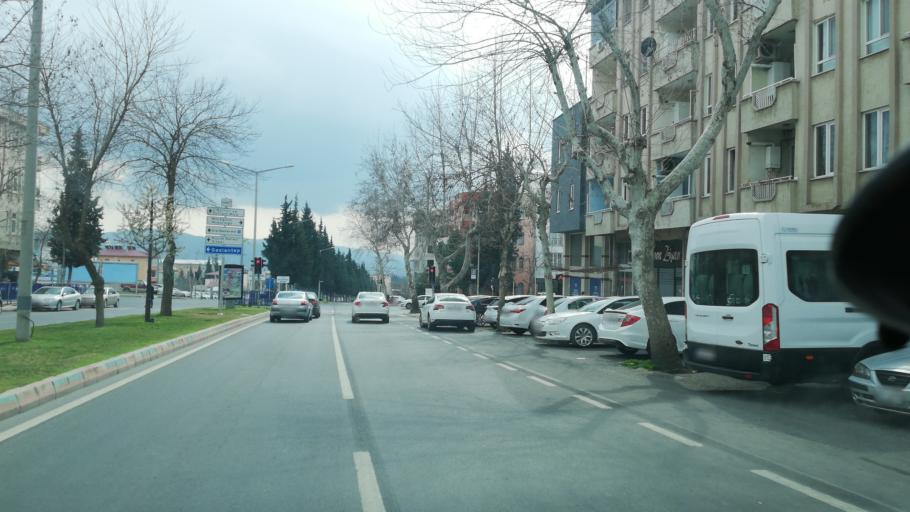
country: TR
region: Kahramanmaras
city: Kahramanmaras
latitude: 37.5725
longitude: 36.9335
